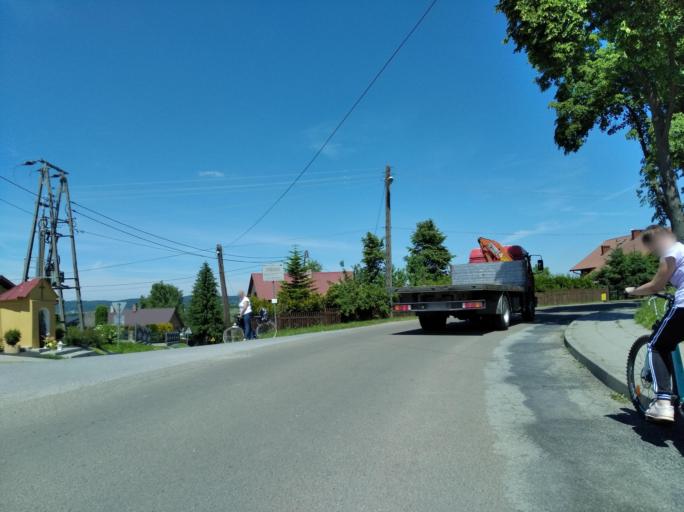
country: PL
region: Subcarpathian Voivodeship
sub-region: Powiat jasielski
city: Tarnowiec
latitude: 49.7310
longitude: 21.5767
